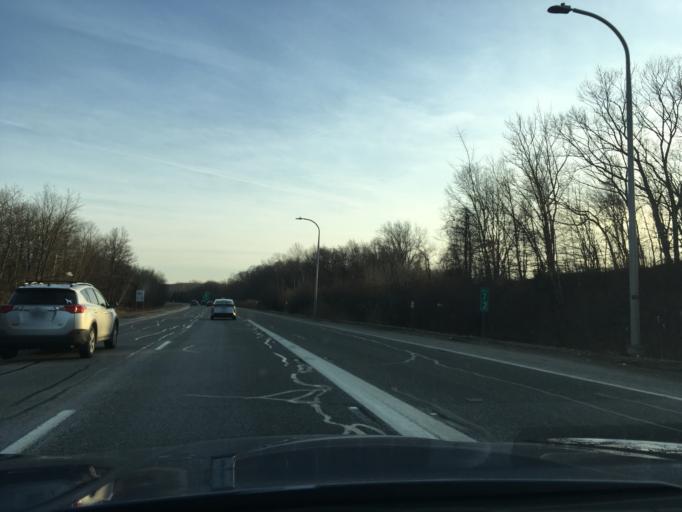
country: US
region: Rhode Island
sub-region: Providence County
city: Johnston
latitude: 41.8014
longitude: -71.5110
